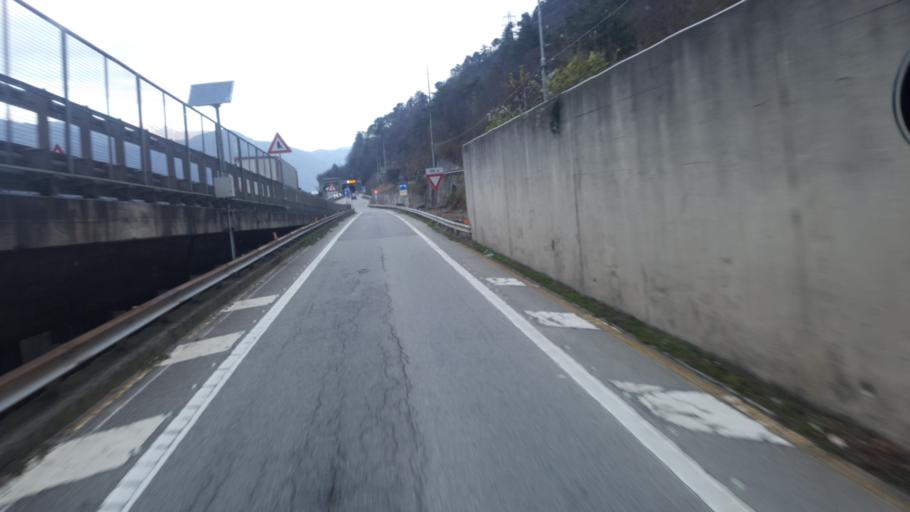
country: IT
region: Lombardy
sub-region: Provincia di Lecco
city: Malgrate
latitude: 45.8810
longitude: 9.3688
